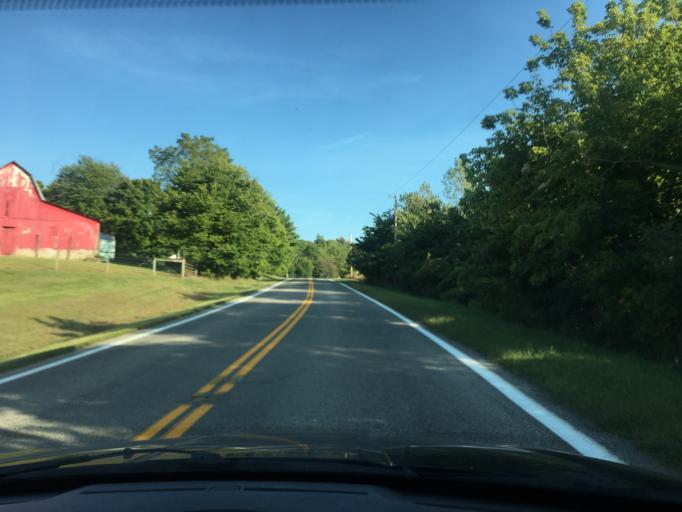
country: US
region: Ohio
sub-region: Logan County
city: West Liberty
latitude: 40.2618
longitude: -83.6621
